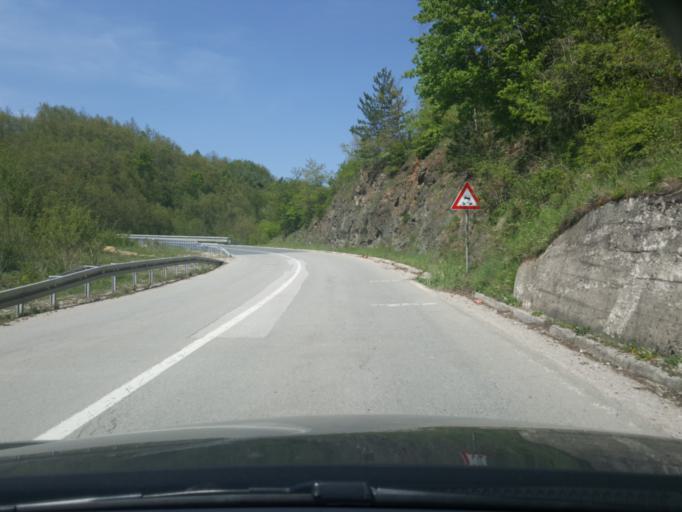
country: RS
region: Central Serbia
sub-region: Zlatiborski Okrug
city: Cajetina
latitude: 43.8078
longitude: 19.6470
